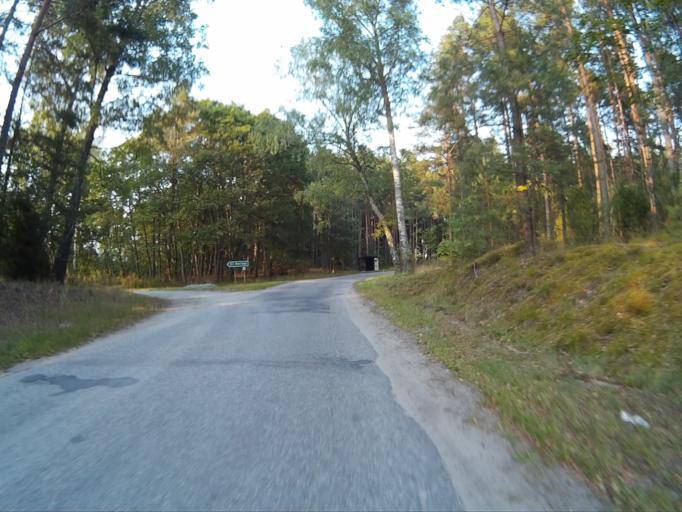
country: PL
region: Pomeranian Voivodeship
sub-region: Powiat chojnicki
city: Czersk
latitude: 53.7135
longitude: 17.9784
